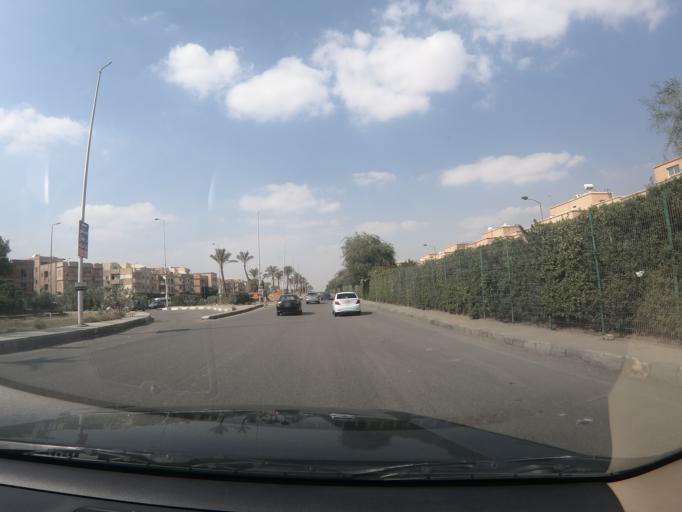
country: EG
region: Muhafazat al Qalyubiyah
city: Al Khankah
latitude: 30.0591
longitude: 31.4751
